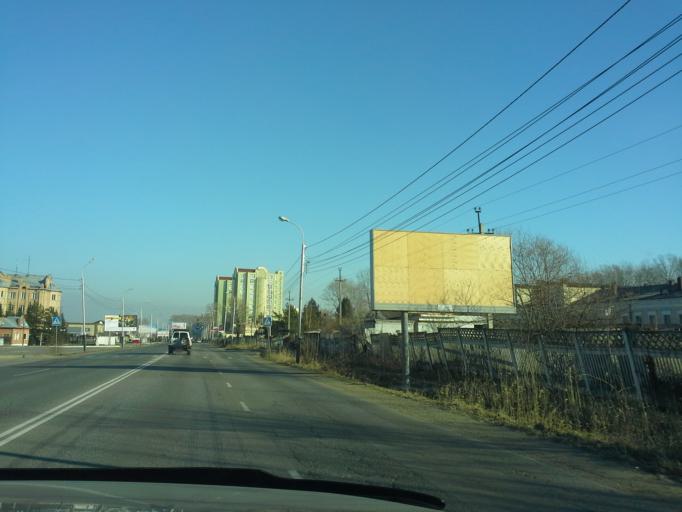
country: RU
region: Khabarovsk Krai
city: Khabarovsk Vtoroy
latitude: 48.4771
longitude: 135.1273
